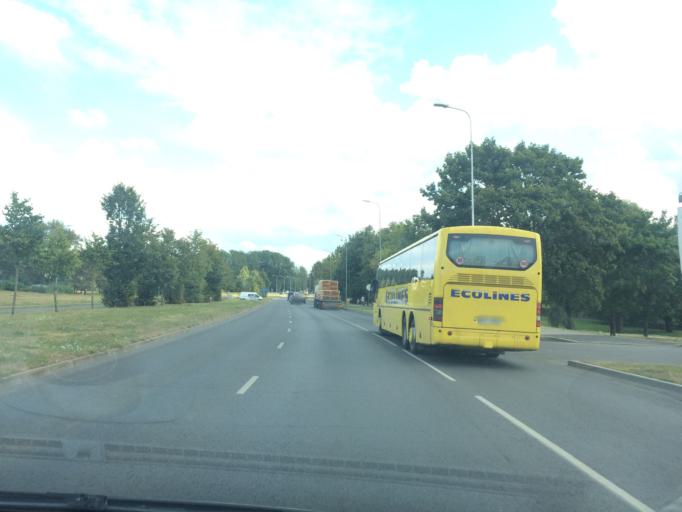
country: LV
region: Kekava
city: Balozi
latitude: 56.9034
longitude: 24.1940
